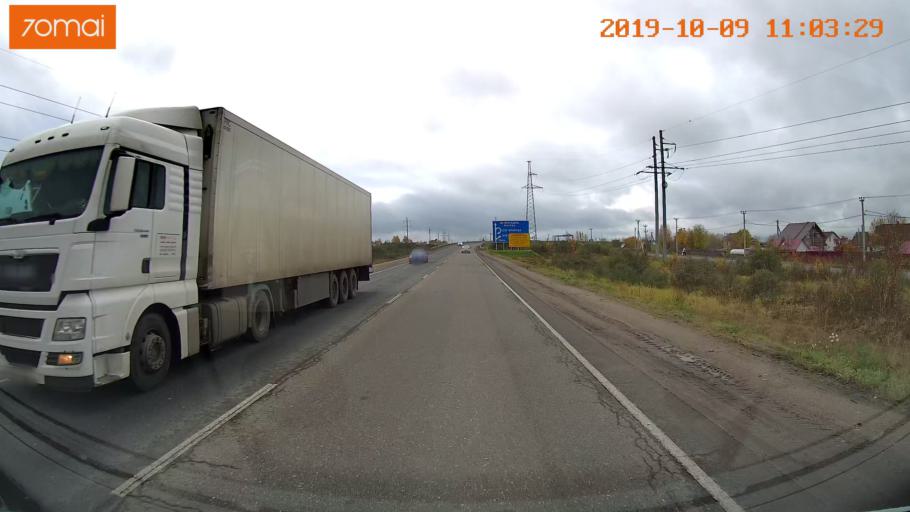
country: RU
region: Vologda
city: Vologda
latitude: 59.2215
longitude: 39.7742
